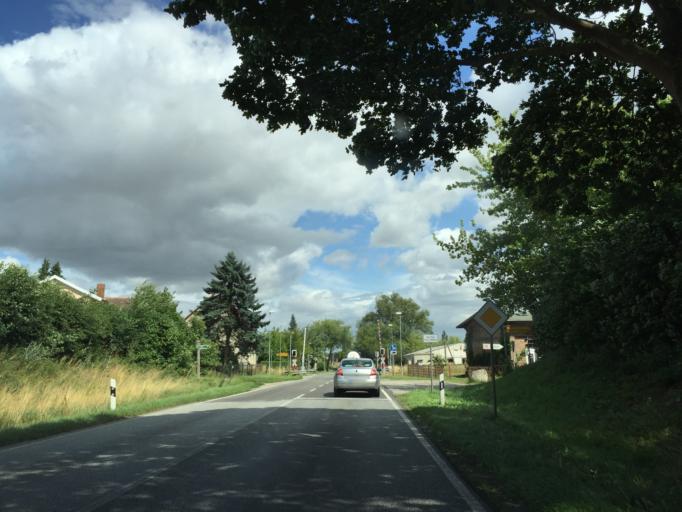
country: DE
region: Mecklenburg-Vorpommern
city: Rosenow
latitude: 53.6251
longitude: 13.0589
